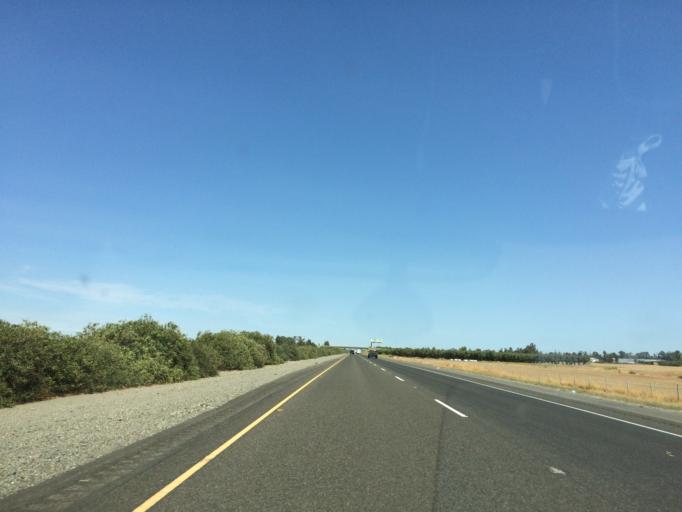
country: US
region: California
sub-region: Glenn County
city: Orland
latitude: 39.6903
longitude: -122.2048
